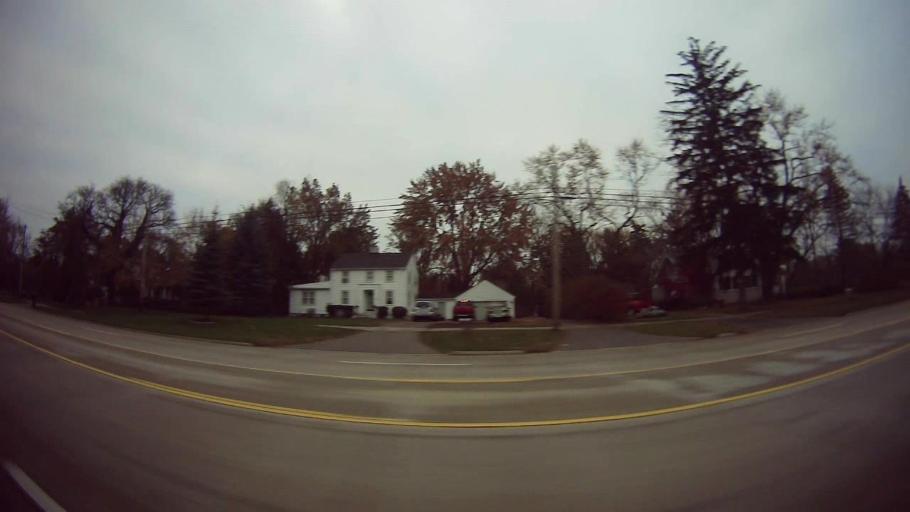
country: US
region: Michigan
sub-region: Oakland County
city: Birmingham
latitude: 42.5610
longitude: -83.1986
